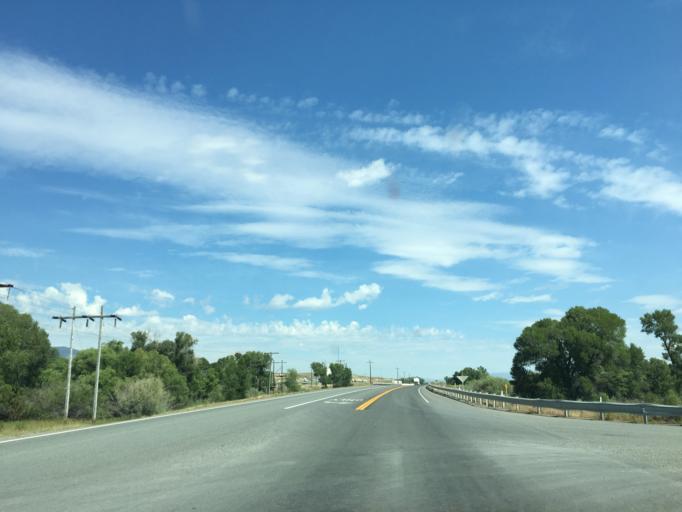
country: US
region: Montana
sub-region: Broadwater County
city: Townsend
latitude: 46.3321
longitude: -111.5300
